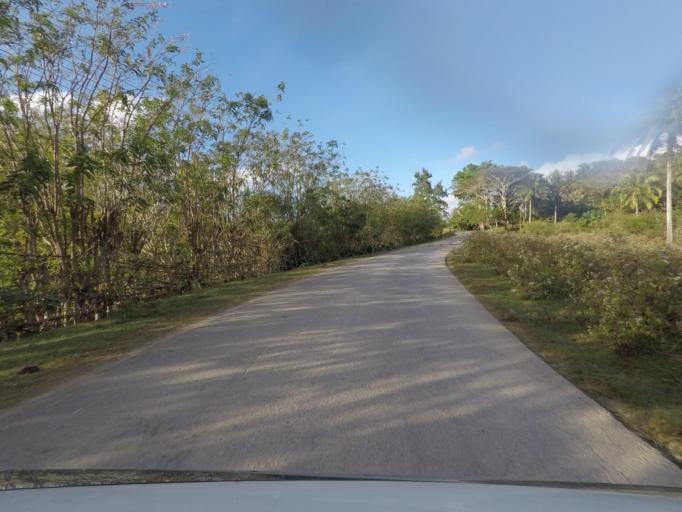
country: TL
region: Lautem
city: Lospalos
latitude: -8.4575
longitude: 126.9999
